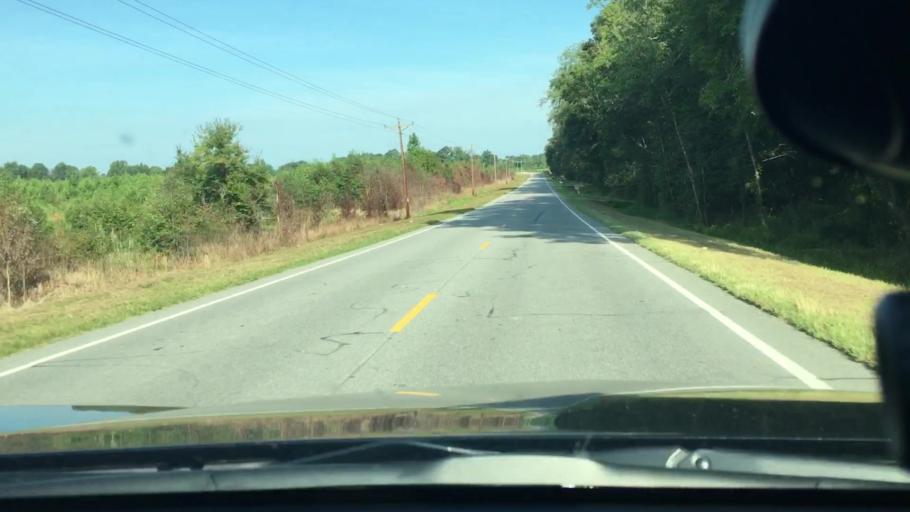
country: US
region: North Carolina
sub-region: Edgecombe County
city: Pinetops
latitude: 35.7855
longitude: -77.6203
